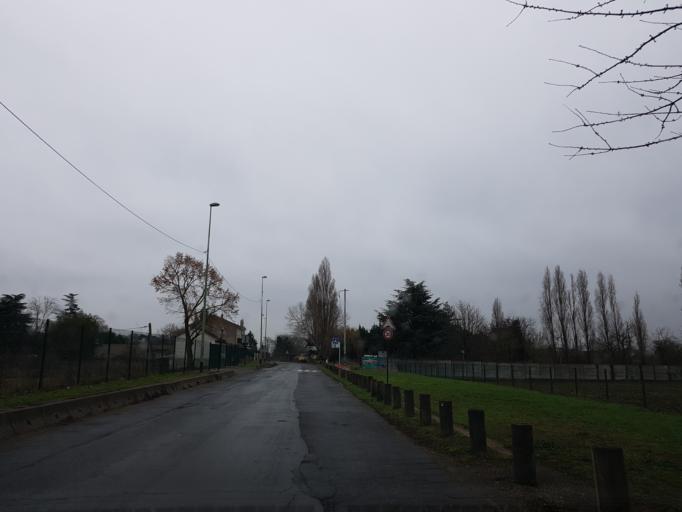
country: FR
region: Ile-de-France
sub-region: Departement du Val-de-Marne
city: Thiais
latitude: 48.7751
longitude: 2.3900
